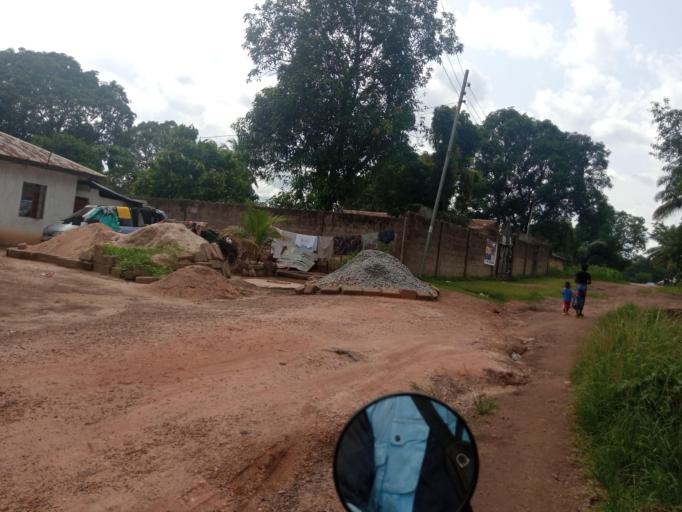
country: SL
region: Southern Province
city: Baoma
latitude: 7.9822
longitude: -11.7295
